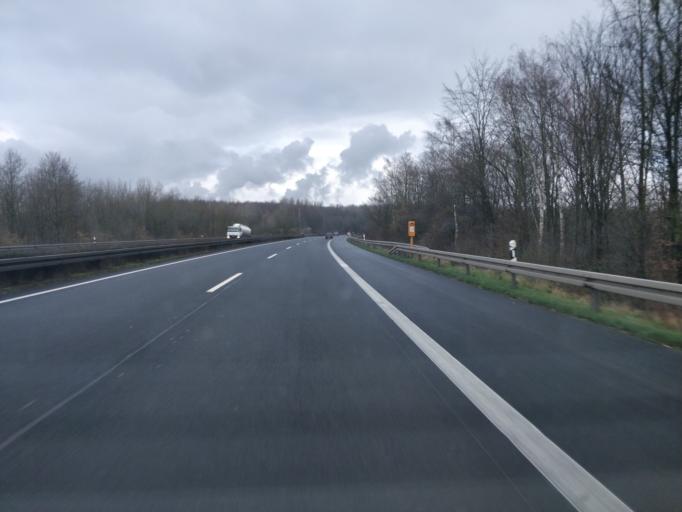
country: DE
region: North Rhine-Westphalia
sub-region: Regierungsbezirk Koln
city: Frechen
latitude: 50.8754
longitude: 6.8021
